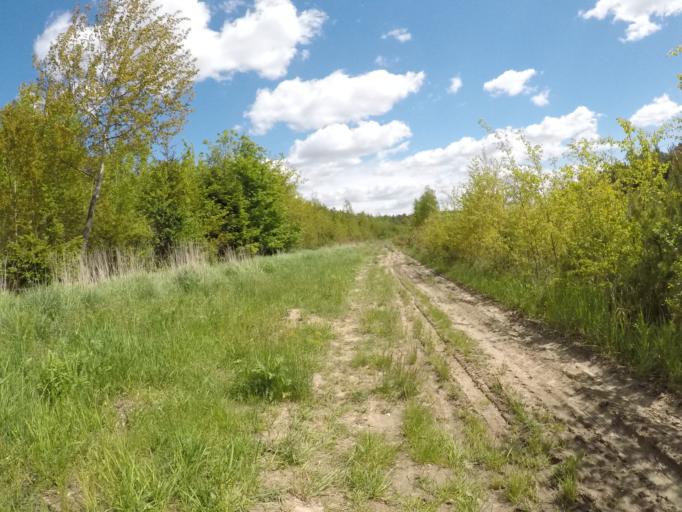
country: PL
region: Swietokrzyskie
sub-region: Powiat kielecki
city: Kostomloty Pierwsze
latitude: 50.9201
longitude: 20.6196
